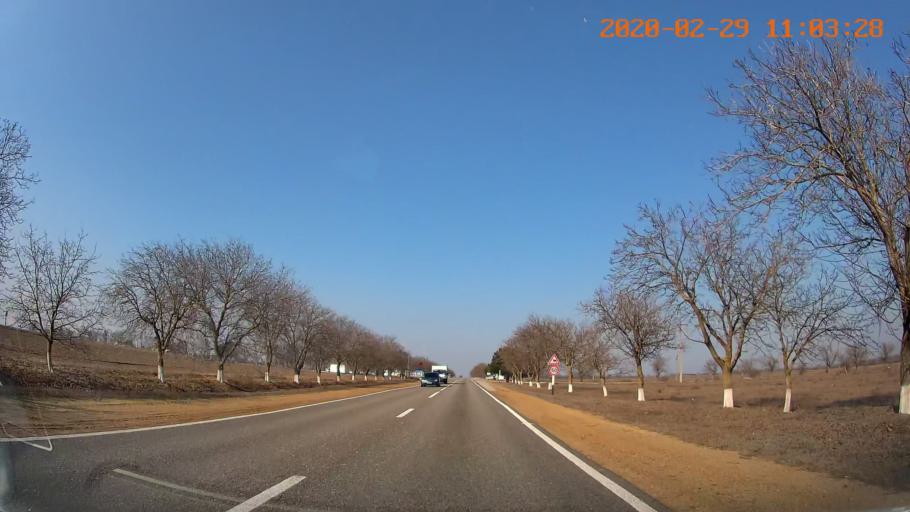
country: MD
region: Criuleni
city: Criuleni
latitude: 47.1798
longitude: 29.2168
